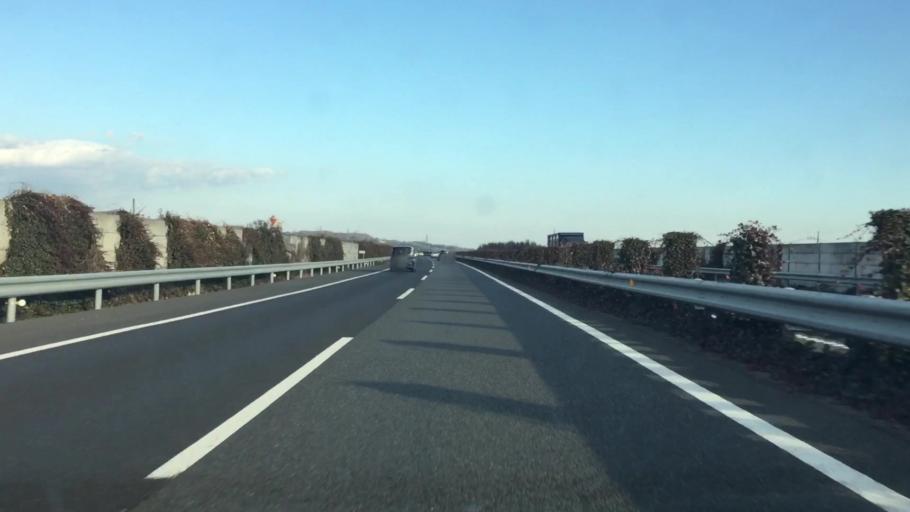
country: JP
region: Gunma
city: Kiryu
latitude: 36.3455
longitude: 139.2923
